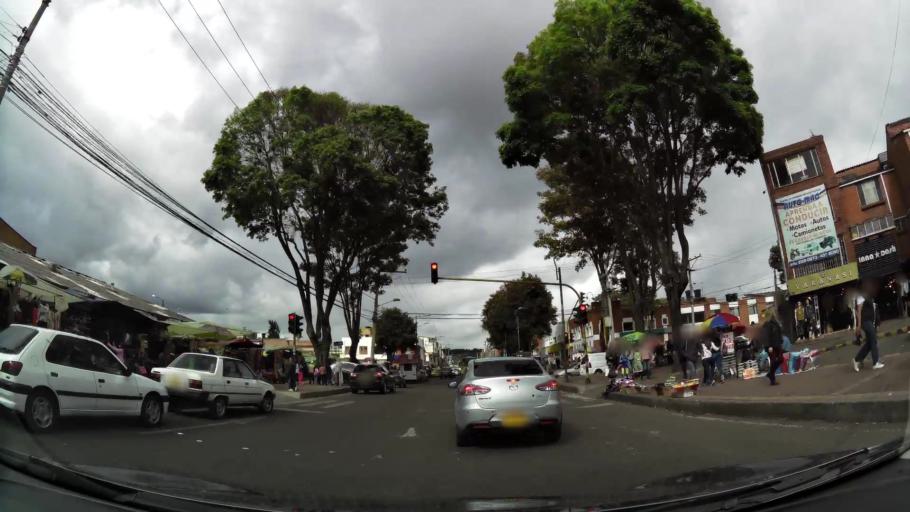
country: CO
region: Bogota D.C.
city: Barrio San Luis
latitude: 4.7081
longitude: -74.1051
